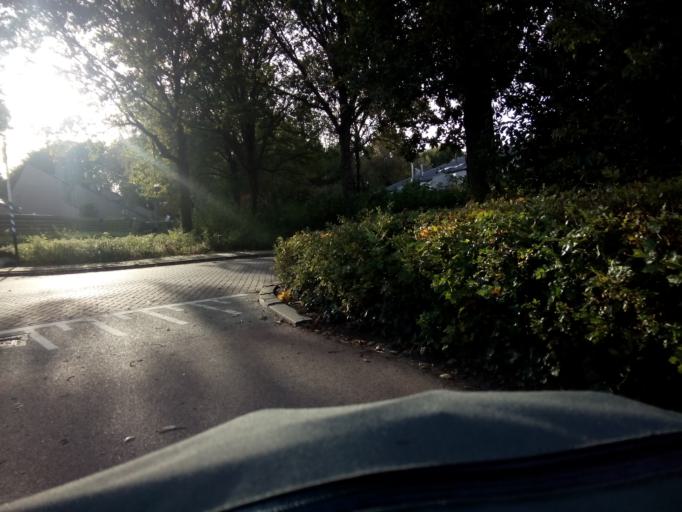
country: NL
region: Drenthe
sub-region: Gemeente Assen
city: Assen
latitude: 52.9829
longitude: 6.5306
